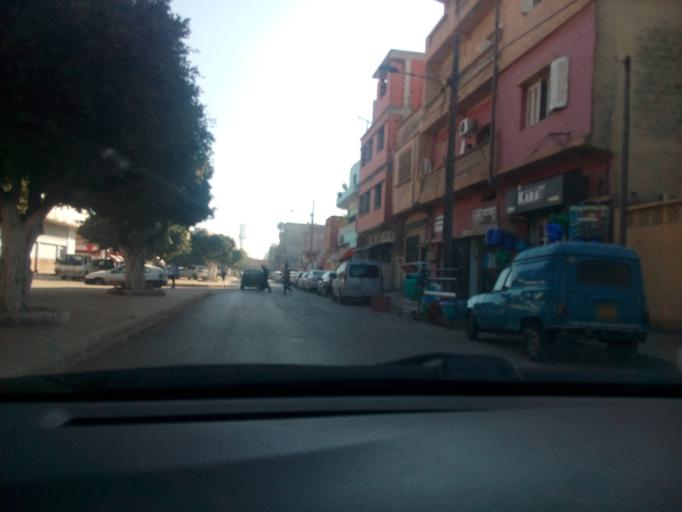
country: DZ
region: Oran
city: Es Senia
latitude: 35.6497
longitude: -0.6261
